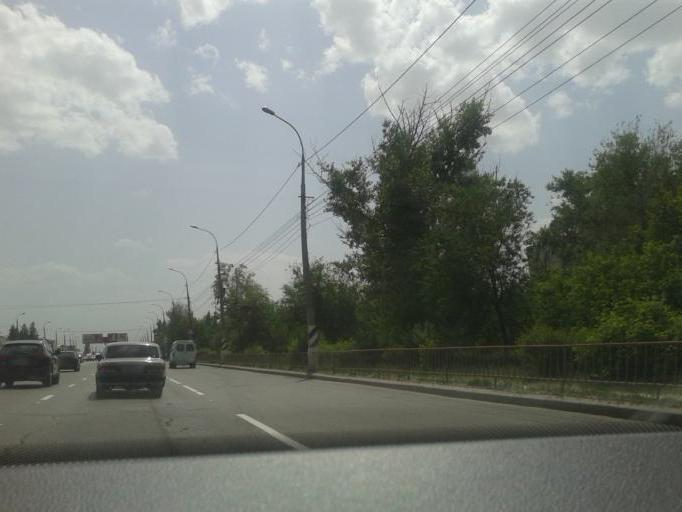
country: RU
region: Volgograd
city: Volgograd
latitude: 48.6512
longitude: 44.4354
